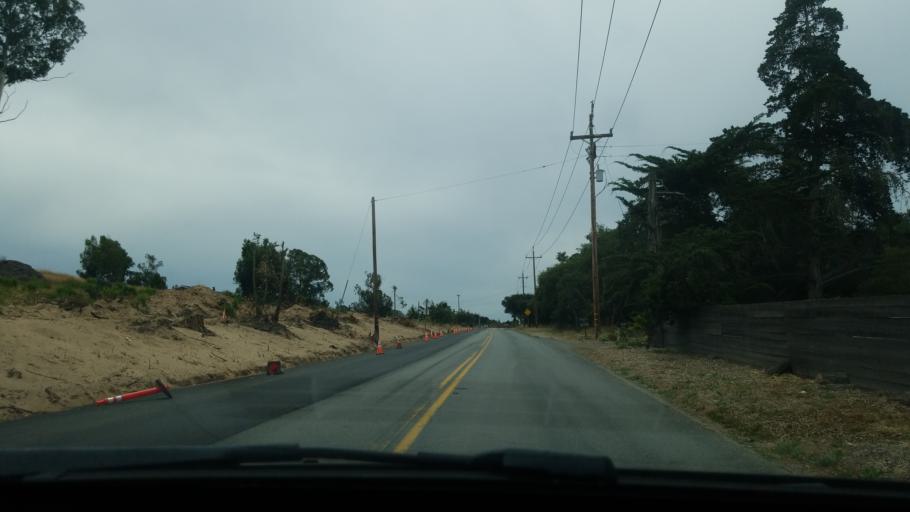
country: US
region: California
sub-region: San Luis Obispo County
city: Callender
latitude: 35.0731
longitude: -120.5405
